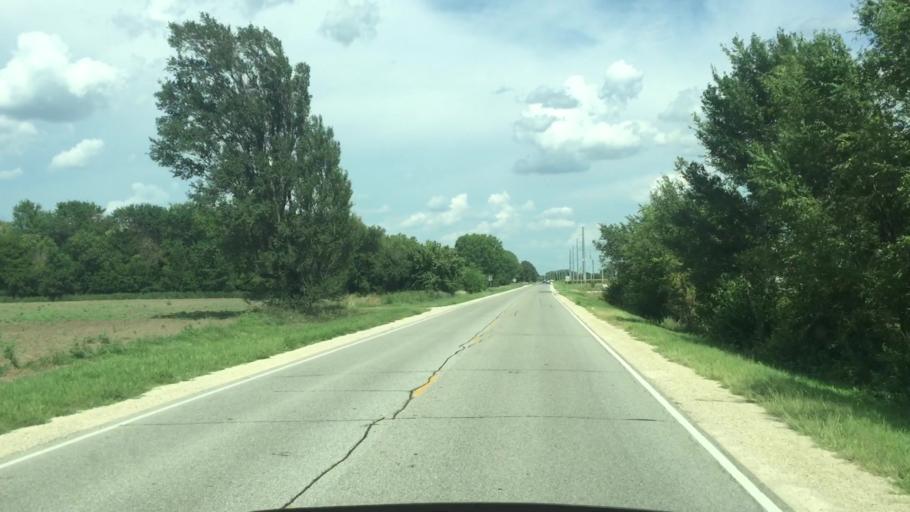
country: US
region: Kansas
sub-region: Sedgwick County
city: Maize
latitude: 37.7810
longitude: -97.4556
